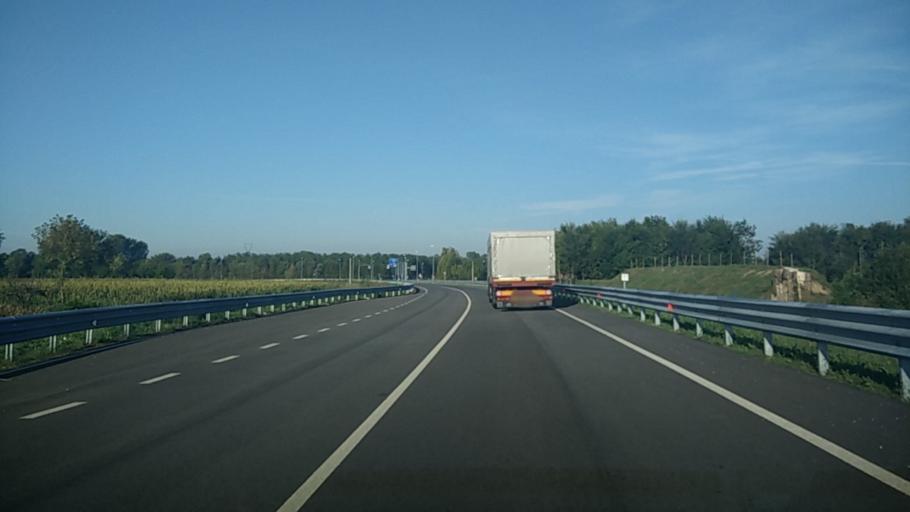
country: IT
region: Veneto
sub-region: Provincia di Venezia
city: Peseggia-Gardigiano
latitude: 45.5510
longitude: 12.1761
